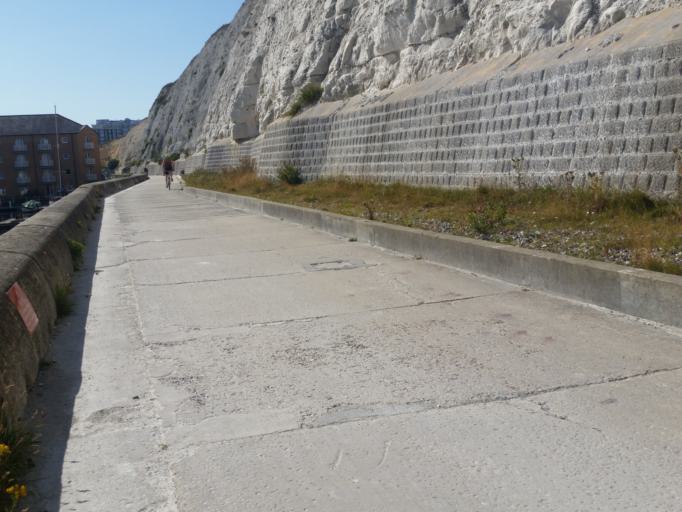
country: GB
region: England
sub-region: Brighton and Hove
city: Rottingdean
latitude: 50.8134
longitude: -0.0987
